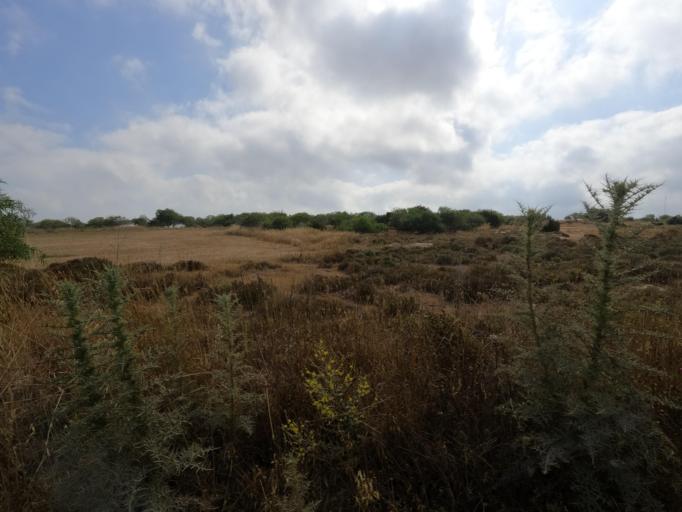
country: CY
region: Ammochostos
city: Ayia Napa
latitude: 35.0133
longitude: 34.0078
